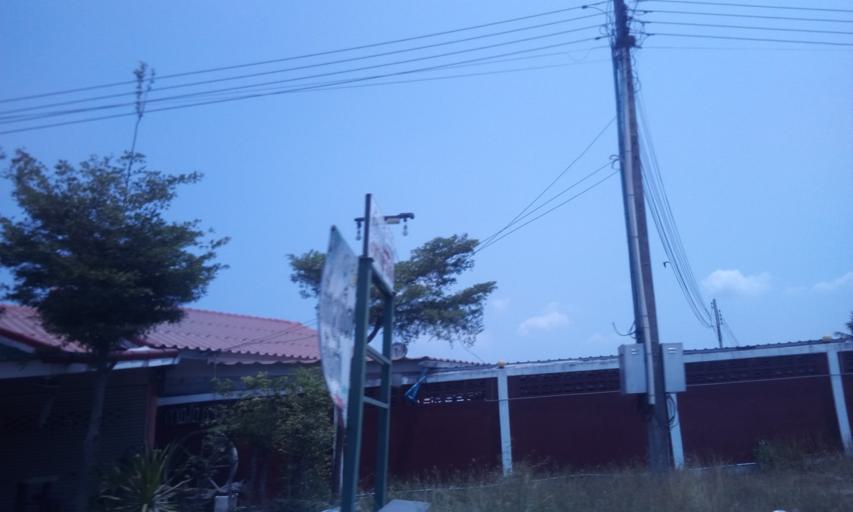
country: TH
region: Chachoengsao
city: Bang Nam Priao
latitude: 13.9471
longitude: 100.9759
